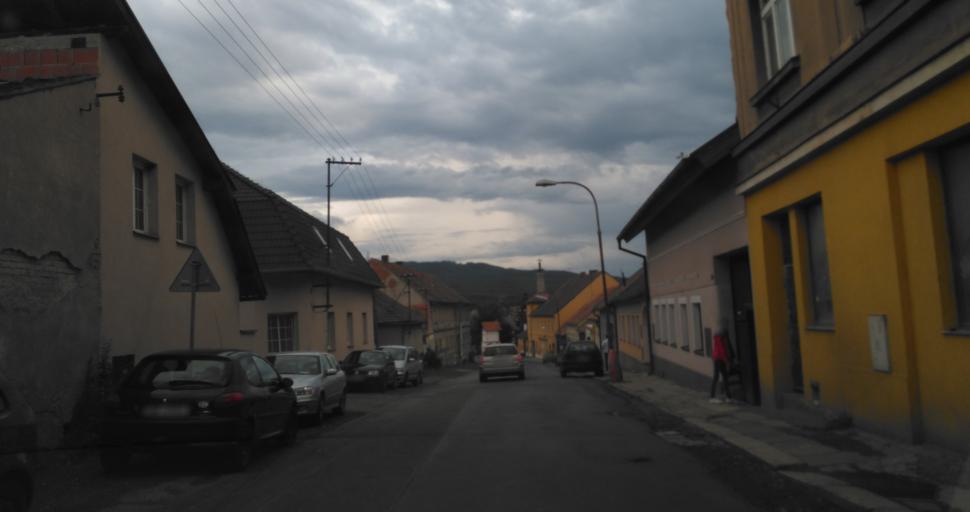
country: CZ
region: Central Bohemia
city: Hostomice
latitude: 49.8248
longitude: 14.0450
